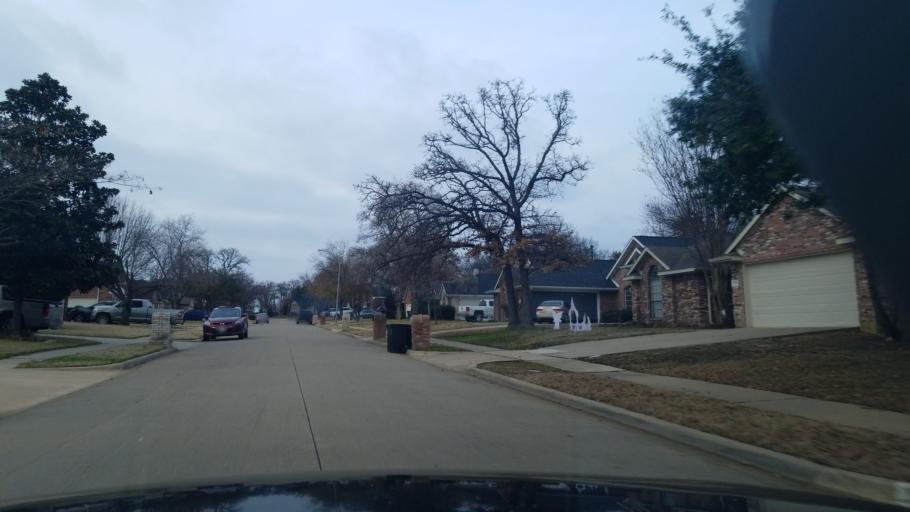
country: US
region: Texas
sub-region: Denton County
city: Corinth
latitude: 33.1399
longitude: -97.0749
